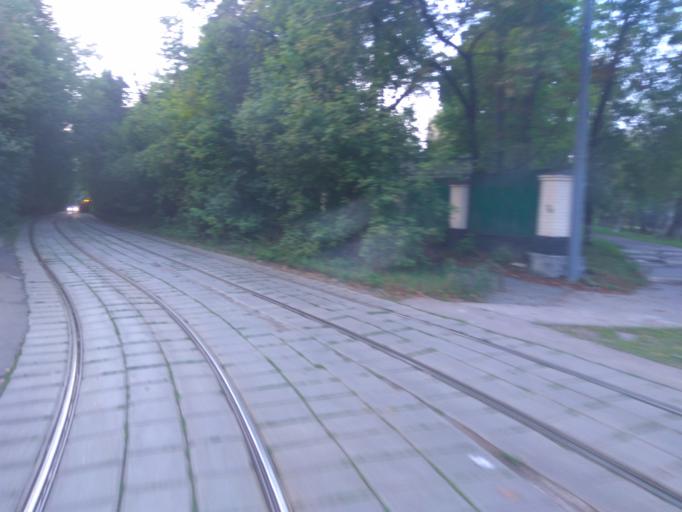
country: RU
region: Moscow
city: Sokol'niki
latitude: 55.8059
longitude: 37.6917
